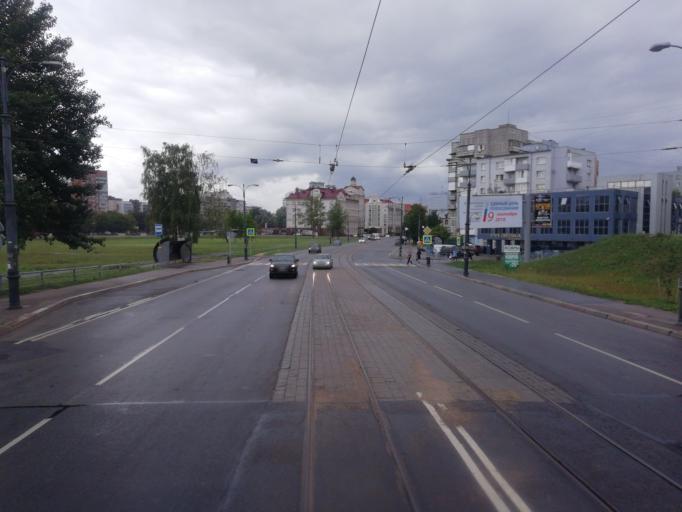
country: RU
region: Kaliningrad
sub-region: Gorod Kaliningrad
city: Kaliningrad
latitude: 54.7001
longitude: 20.5179
